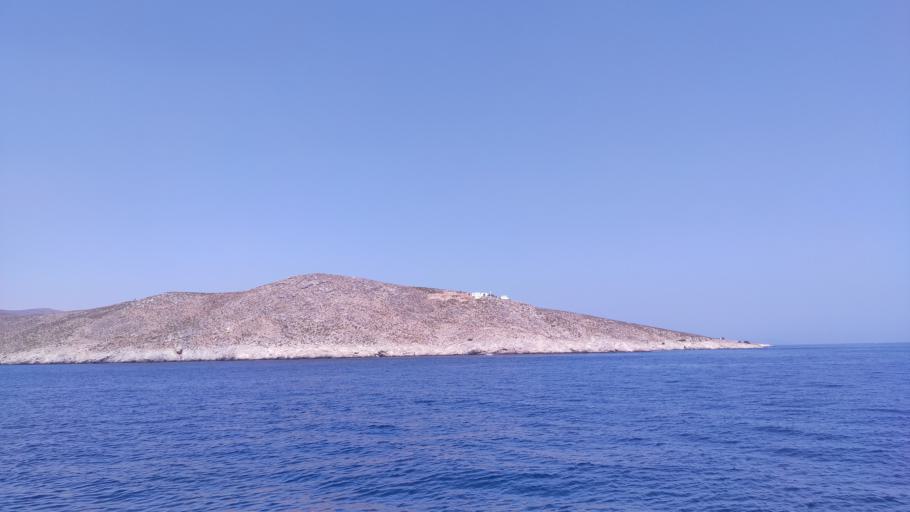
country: GR
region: South Aegean
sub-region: Nomos Dodekanisou
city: Kalymnos
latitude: 36.9400
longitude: 27.0533
